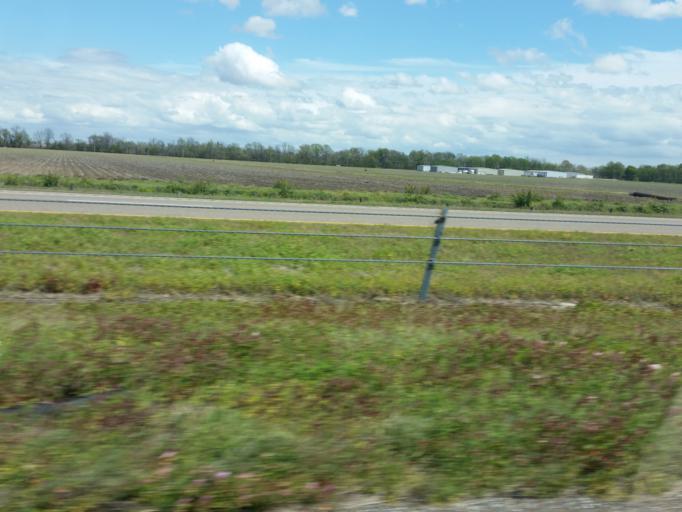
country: US
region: Arkansas
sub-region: Crittenden County
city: Marion
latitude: 35.2518
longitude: -90.2222
